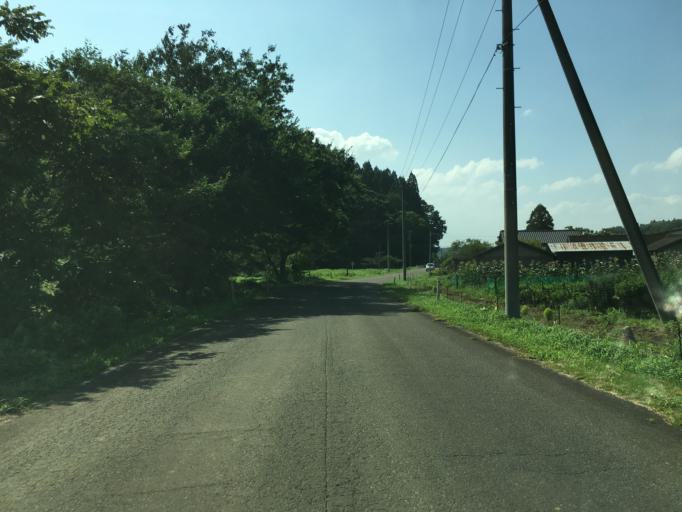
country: JP
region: Miyagi
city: Marumori
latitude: 37.8892
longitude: 140.8386
